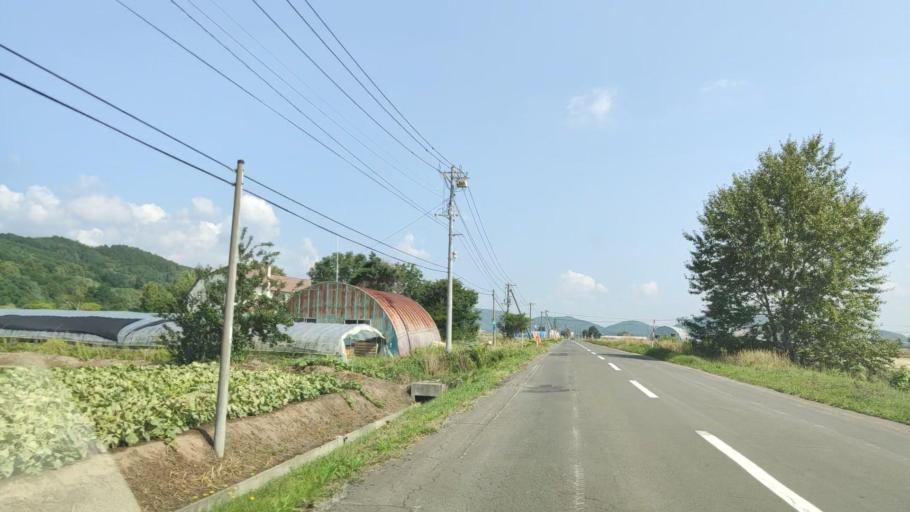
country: JP
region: Hokkaido
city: Shimo-furano
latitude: 43.3793
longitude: 142.3907
